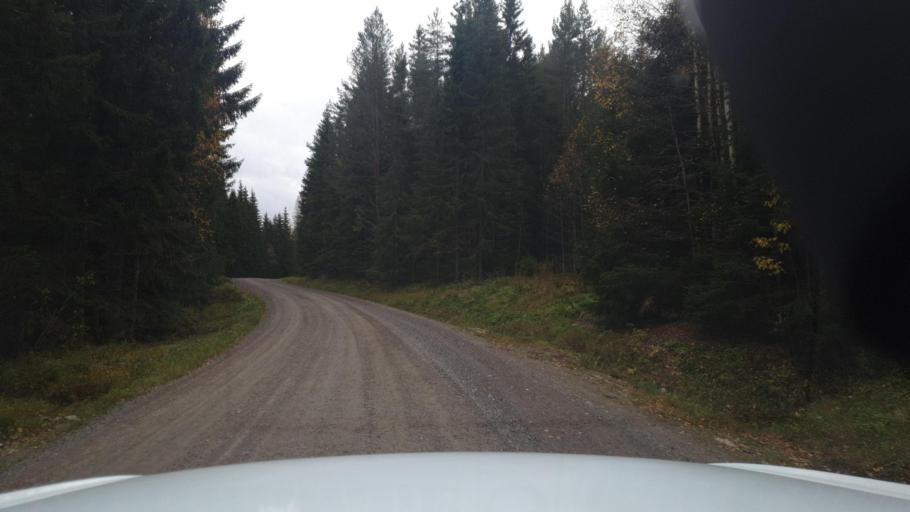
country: SE
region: Vaermland
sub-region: Arvika Kommun
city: Arvika
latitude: 59.9589
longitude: 12.6589
